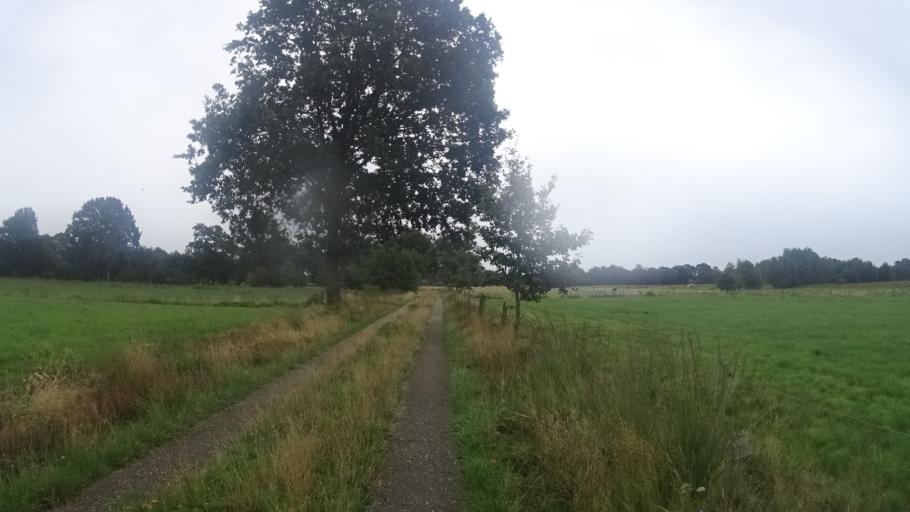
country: DE
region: Schleswig-Holstein
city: Heede
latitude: 53.7595
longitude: 9.7982
